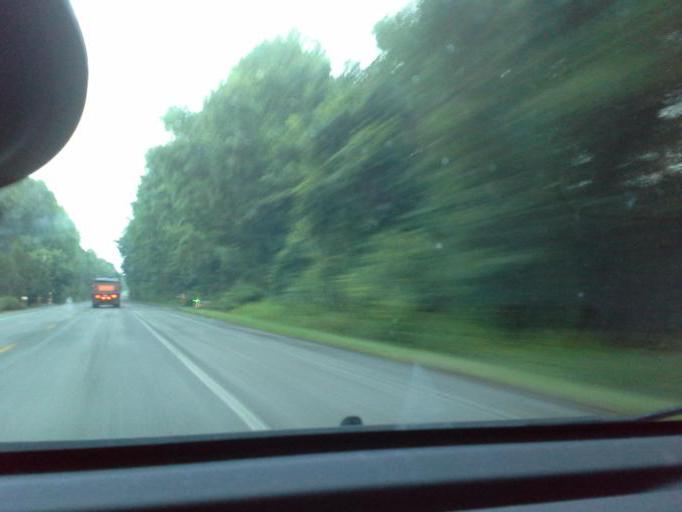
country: US
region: Maryland
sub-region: Calvert County
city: Owings
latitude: 38.7606
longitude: -76.5968
